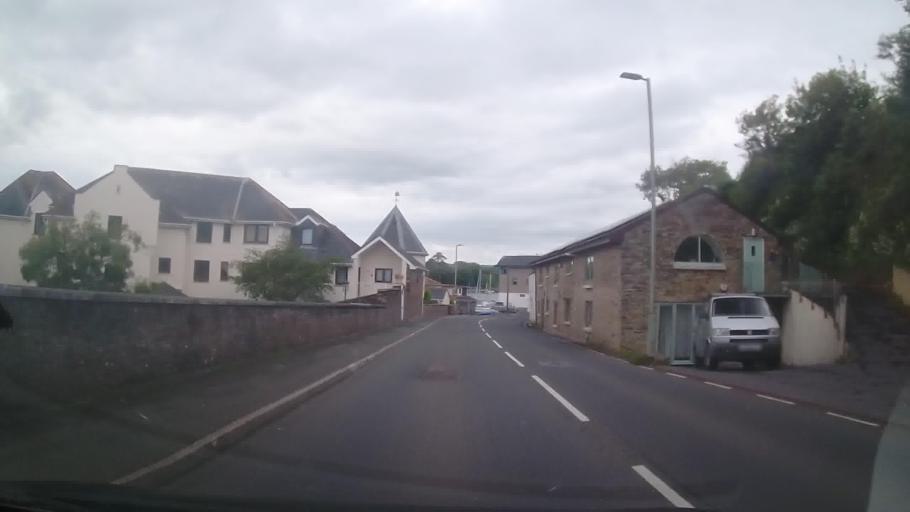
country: GB
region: England
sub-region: Devon
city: Kingsbridge
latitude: 50.2757
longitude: -3.7718
